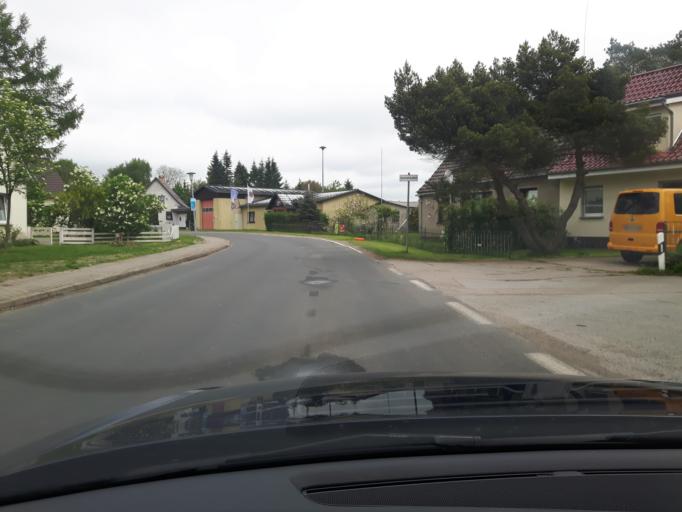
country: DE
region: Mecklenburg-Vorpommern
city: Tribsees
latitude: 54.1629
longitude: 12.7250
